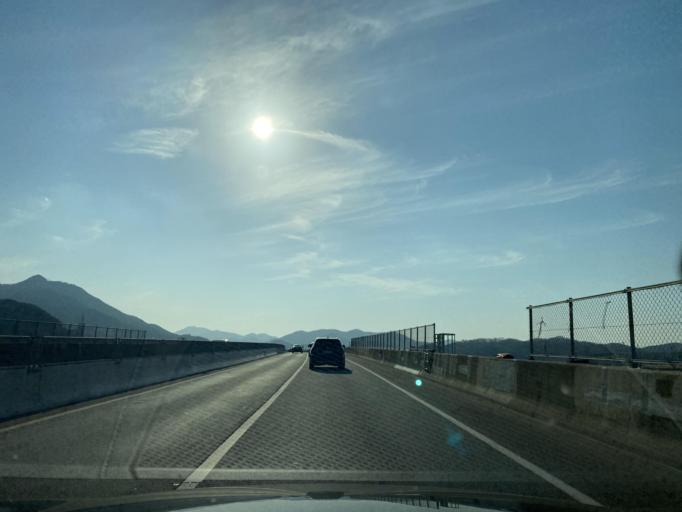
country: KR
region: Chungcheongnam-do
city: Asan
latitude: 36.7728
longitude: 127.0429
